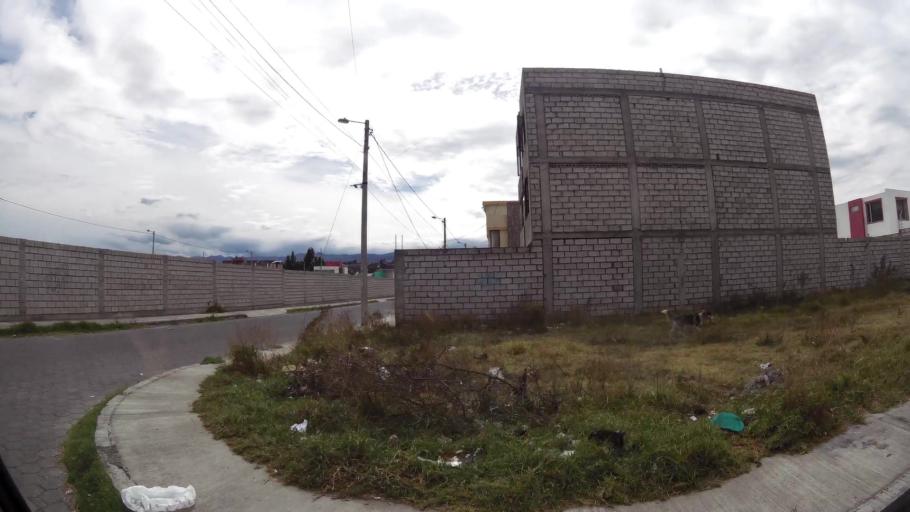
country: EC
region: Cotopaxi
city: Latacunga
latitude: -0.9218
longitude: -78.6223
